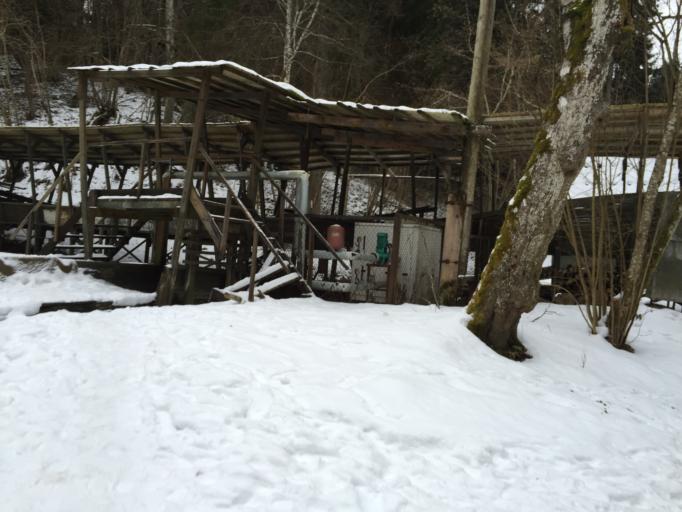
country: LV
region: Seja
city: Loja
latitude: 57.1443
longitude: 24.6810
